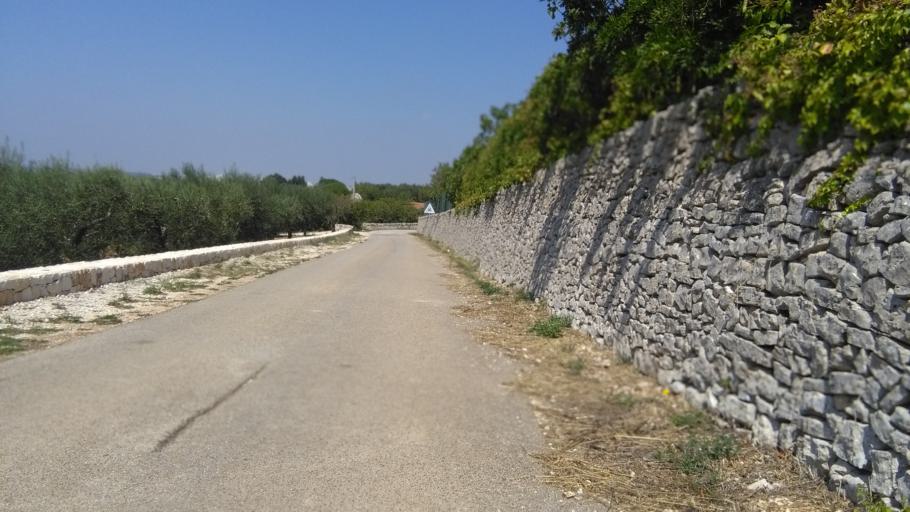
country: IT
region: Apulia
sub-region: Provincia di Bari
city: Noci
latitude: 40.8184
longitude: 17.1634
